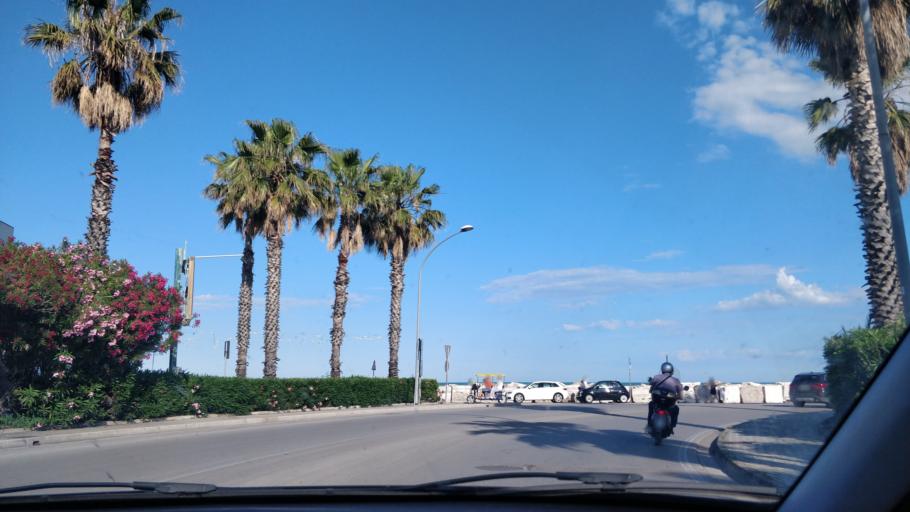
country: IT
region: The Marches
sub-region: Provincia di Ascoli Piceno
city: Grottammare
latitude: 42.9521
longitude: 13.8882
